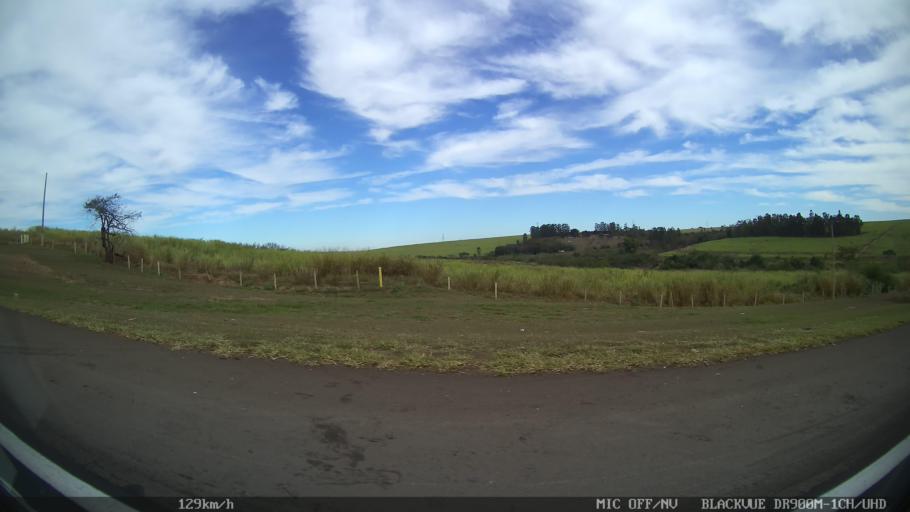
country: BR
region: Sao Paulo
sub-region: Santa Adelia
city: Santa Adelia
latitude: -21.3267
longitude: -48.8041
